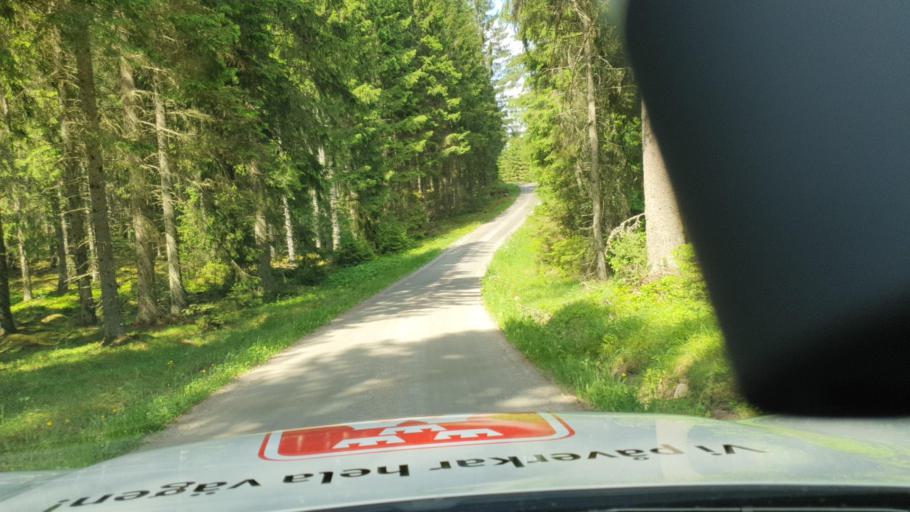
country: SE
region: Vaestra Goetaland
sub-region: Falkopings Kommun
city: Falkoeping
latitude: 58.0506
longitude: 13.6634
